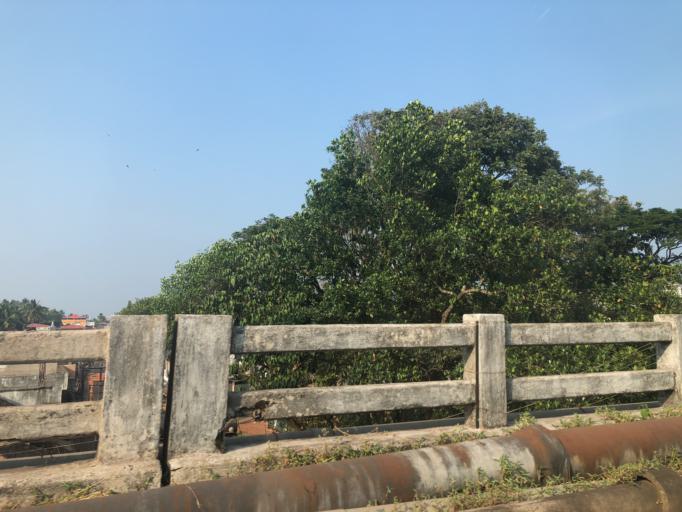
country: IN
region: Karnataka
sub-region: Dakshina Kannada
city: Ullal
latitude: 12.8146
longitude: 74.8573
